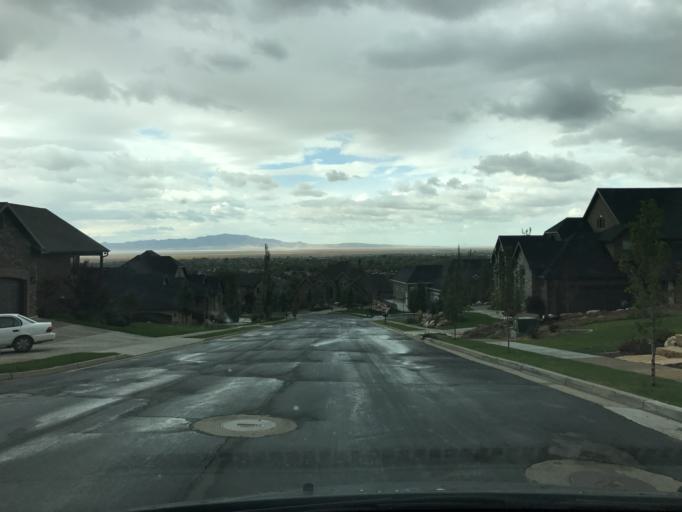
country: US
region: Utah
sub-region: Davis County
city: Fruit Heights
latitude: 41.0144
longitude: -111.8995
